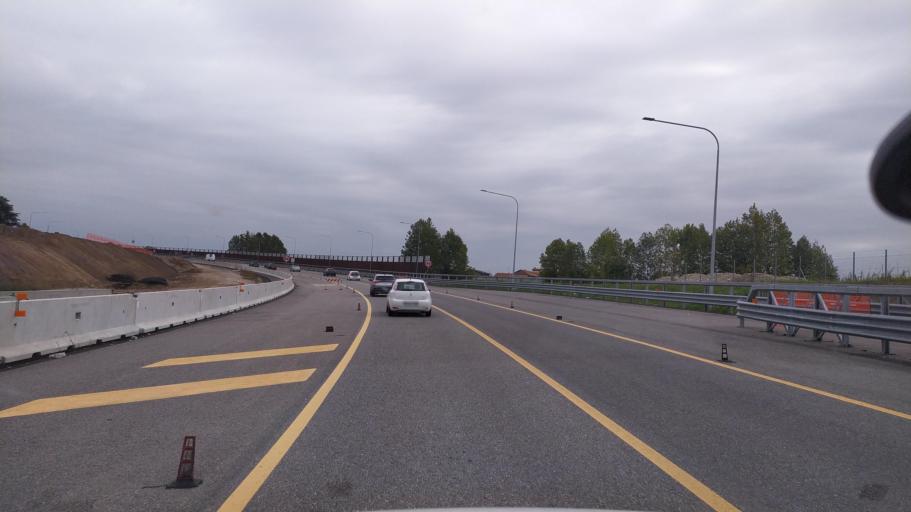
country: IT
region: Lombardy
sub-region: Citta metropolitana di Milano
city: Novate Milanese
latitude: 45.5434
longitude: 9.1468
